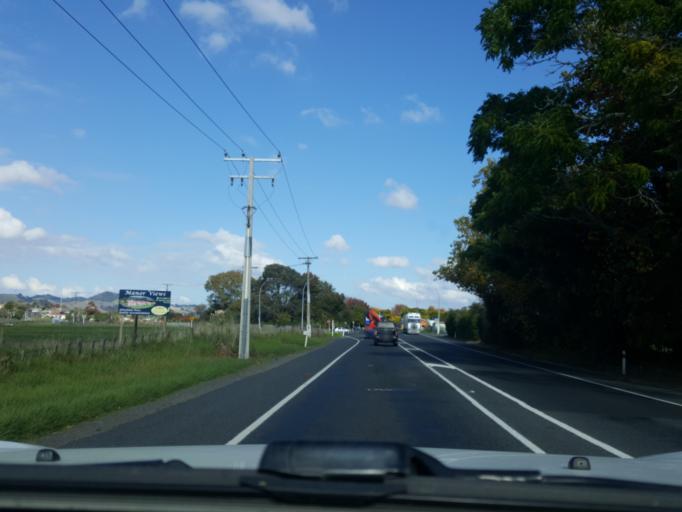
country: NZ
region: Waikato
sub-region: Waikato District
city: Te Kauwhata
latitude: -37.5269
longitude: 175.1598
